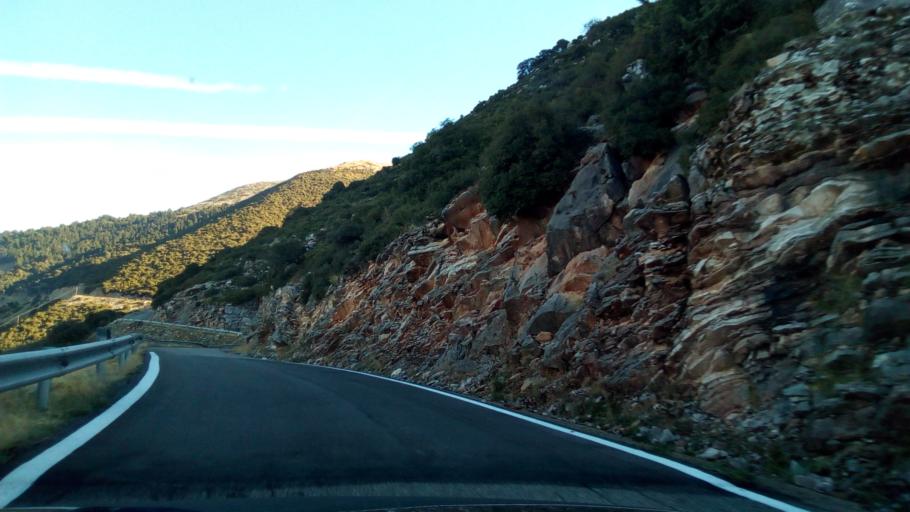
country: GR
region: West Greece
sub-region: Nomos Aitolias kai Akarnanias
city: Nafpaktos
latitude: 38.5136
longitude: 21.8463
